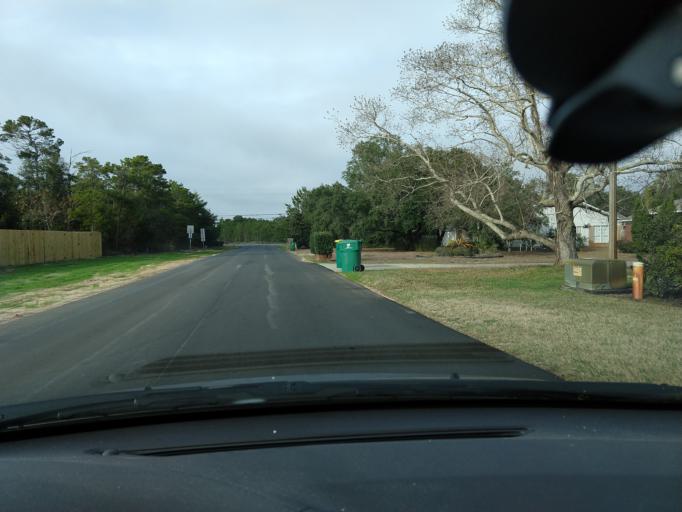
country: US
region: Florida
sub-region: Santa Rosa County
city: Woodlawn Beach
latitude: 30.4011
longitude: -86.9399
